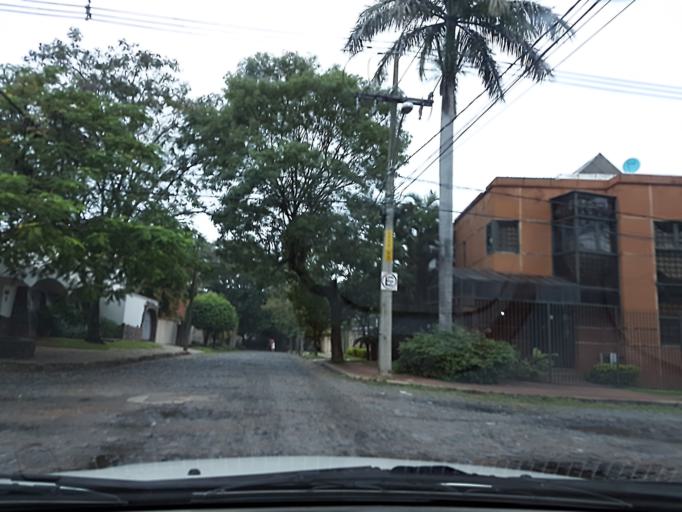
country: PY
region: Asuncion
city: Asuncion
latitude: -25.2830
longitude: -57.5827
